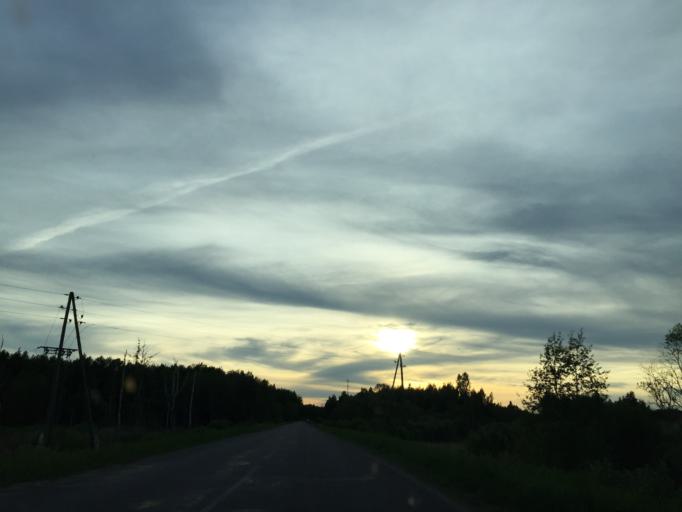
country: LV
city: Tireli
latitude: 56.8278
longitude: 23.5656
